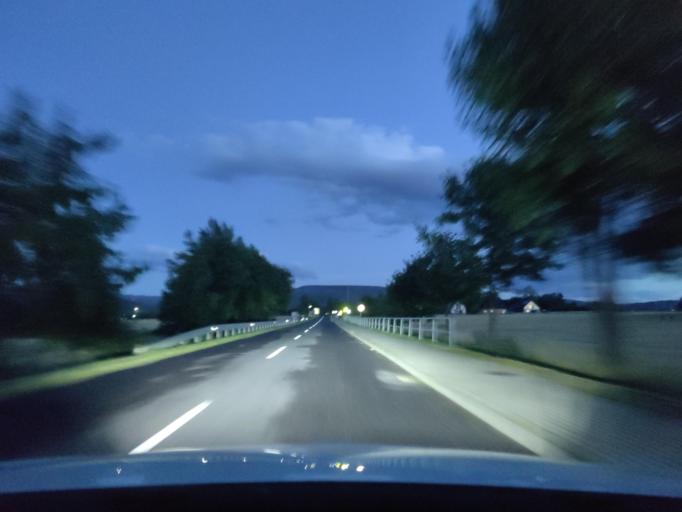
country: CZ
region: Olomoucky
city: Zlate Hory
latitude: 50.2869
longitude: 17.3895
